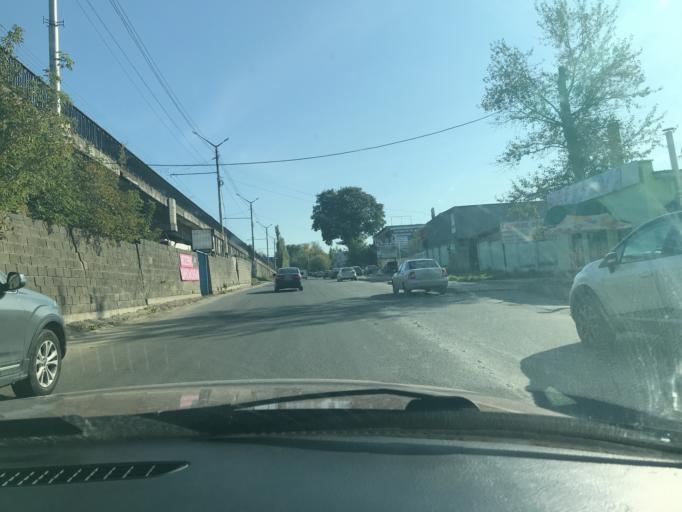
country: RU
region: Kaluga
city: Kaluga
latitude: 54.5559
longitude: 36.2647
